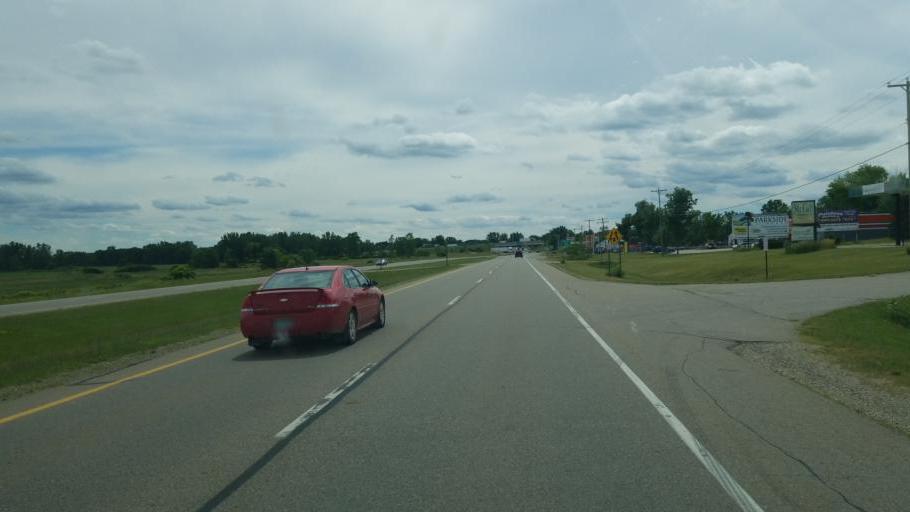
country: US
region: Michigan
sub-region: Eaton County
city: Charlotte
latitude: 42.5795
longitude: -84.8127
